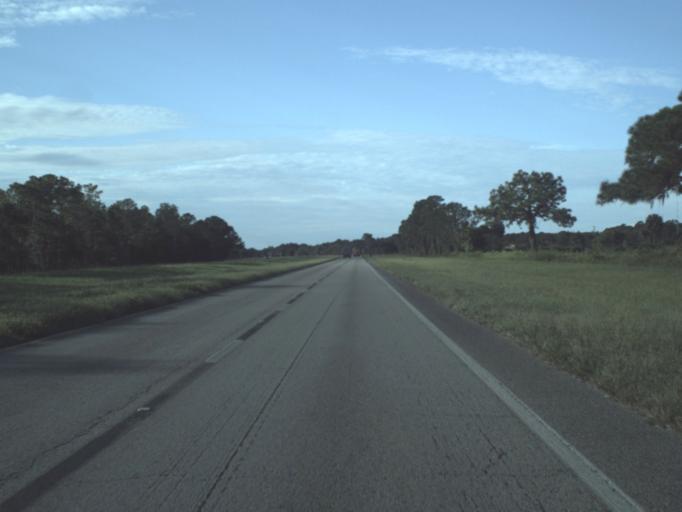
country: US
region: Florida
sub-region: Highlands County
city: Placid Lakes
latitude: 27.0394
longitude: -81.3419
